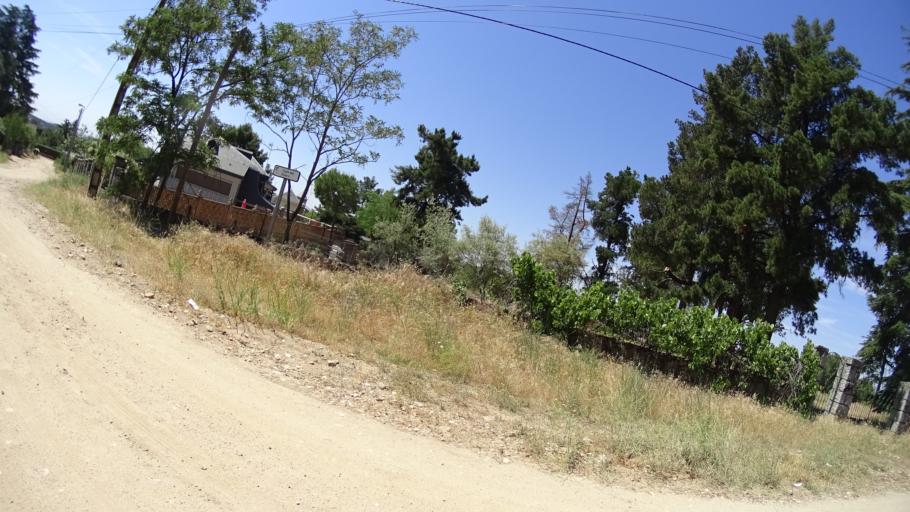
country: ES
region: Madrid
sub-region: Provincia de Madrid
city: Colmenarejo
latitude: 40.5538
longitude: -4.0065
